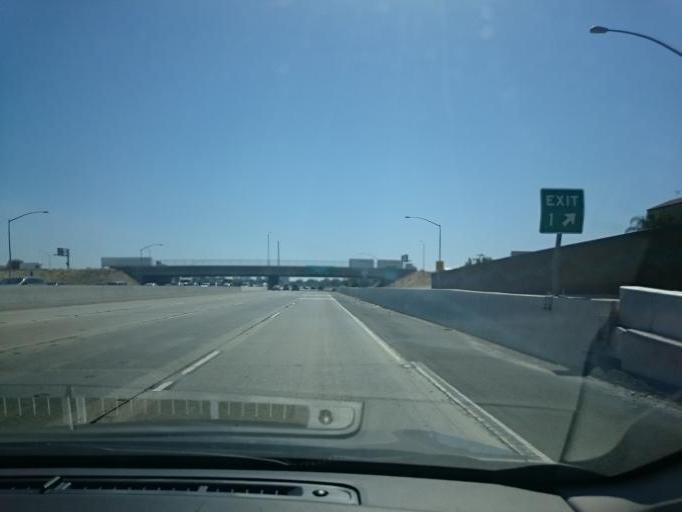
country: US
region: California
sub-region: Yolo County
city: West Sacramento
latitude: 38.5748
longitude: -121.5509
